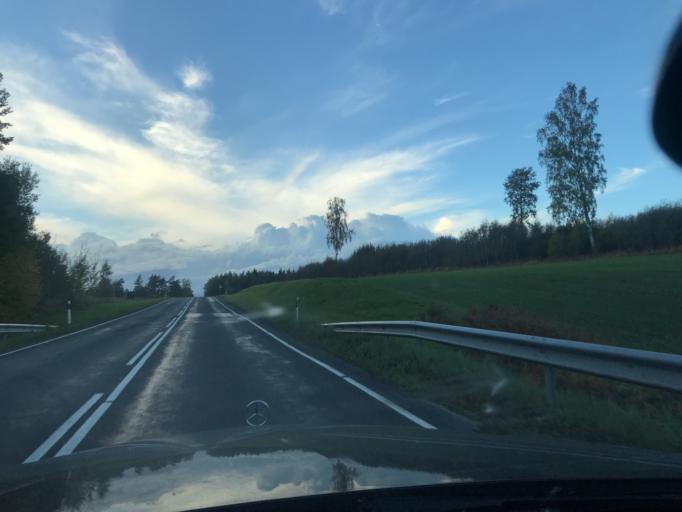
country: EE
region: Vorumaa
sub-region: Antsla vald
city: Vana-Antsla
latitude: 57.8711
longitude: 26.5960
